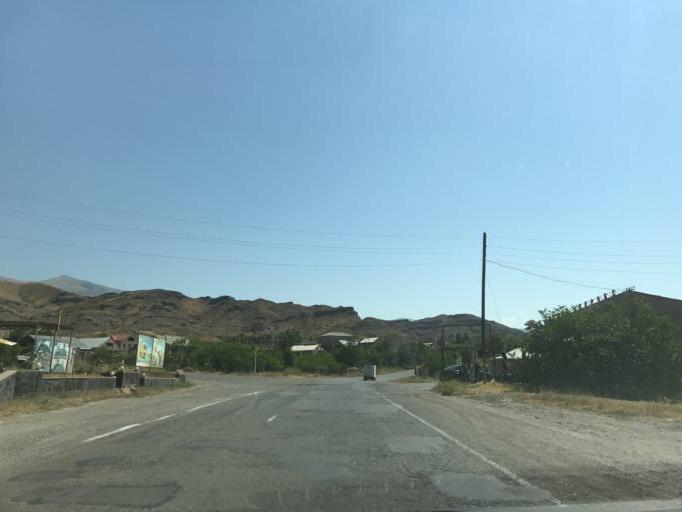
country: AM
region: Vayots' Dzori Marz
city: Yeghegnadzor
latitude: 39.7568
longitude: 45.3423
